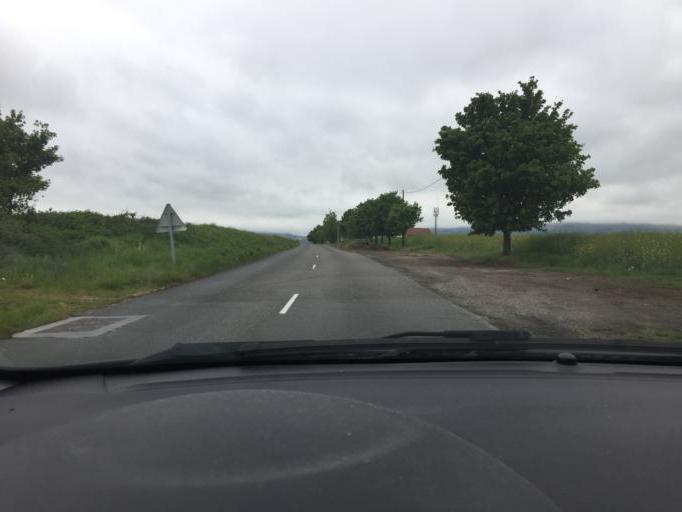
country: FR
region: Rhone-Alpes
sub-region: Departement du Rhone
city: Mornant
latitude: 45.5892
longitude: 4.6629
